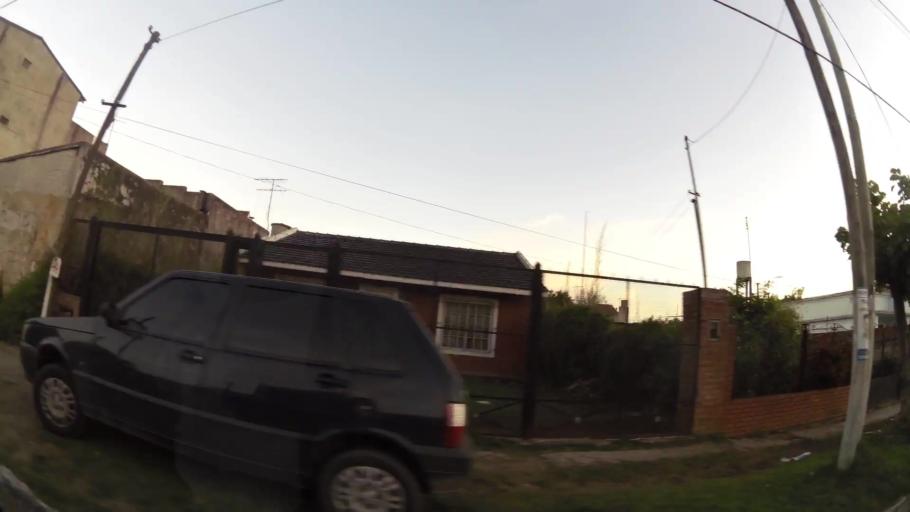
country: AR
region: Buenos Aires
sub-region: Partido de Quilmes
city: Quilmes
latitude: -34.7765
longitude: -58.2104
